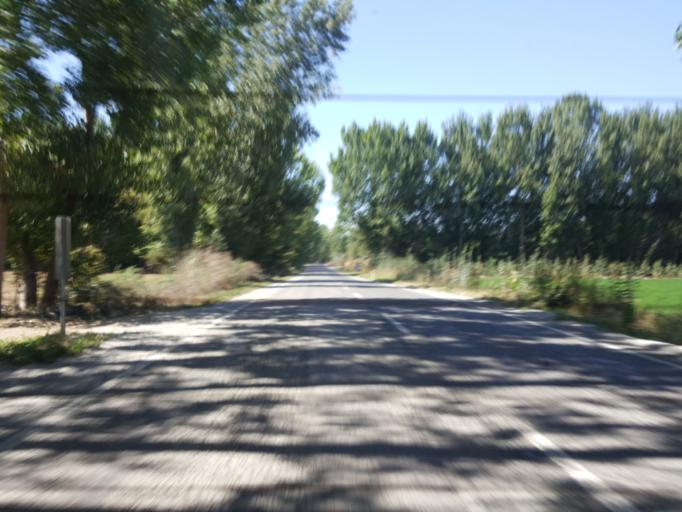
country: TR
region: Tokat
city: Pazar
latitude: 40.2713
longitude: 36.2516
